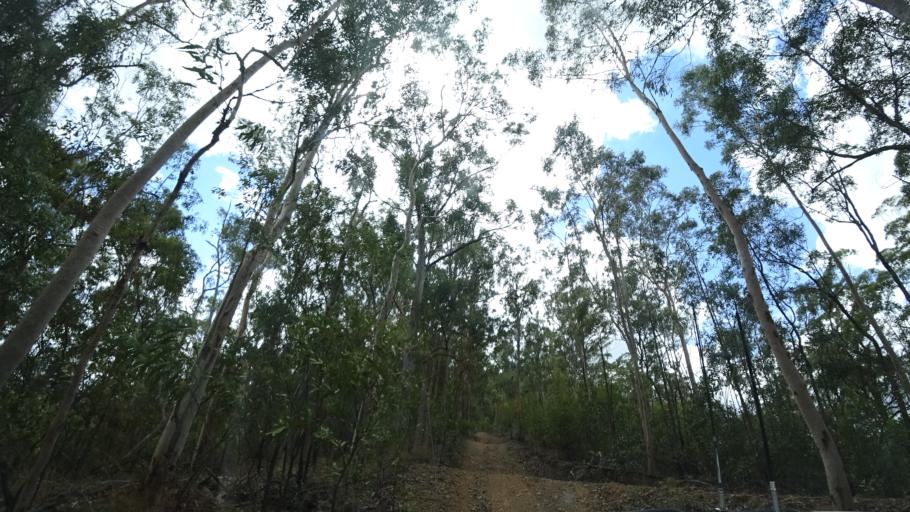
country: AU
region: Queensland
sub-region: Moreton Bay
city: Highvale
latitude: -27.4093
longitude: 152.7401
